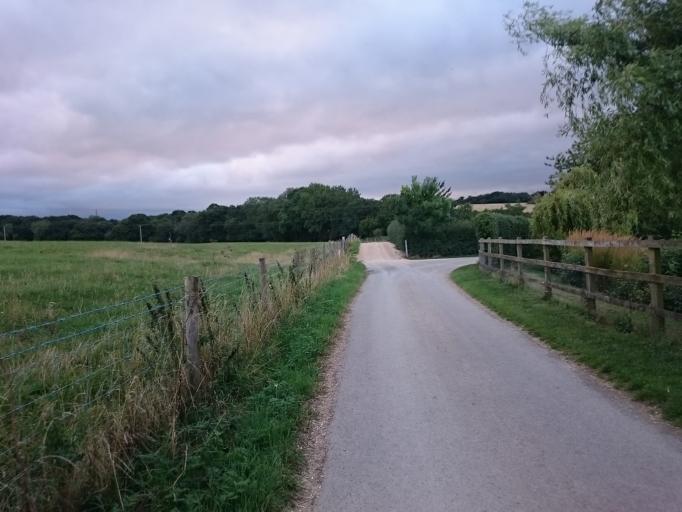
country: GB
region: England
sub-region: Oxfordshire
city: Boars Hill
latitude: 51.7258
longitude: -1.2863
